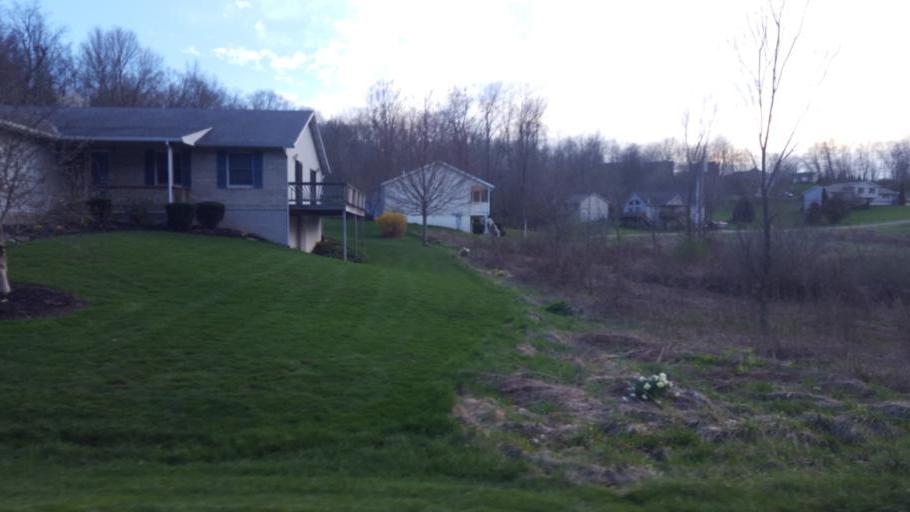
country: US
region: Ohio
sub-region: Knox County
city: Danville
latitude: 40.4550
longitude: -82.3292
